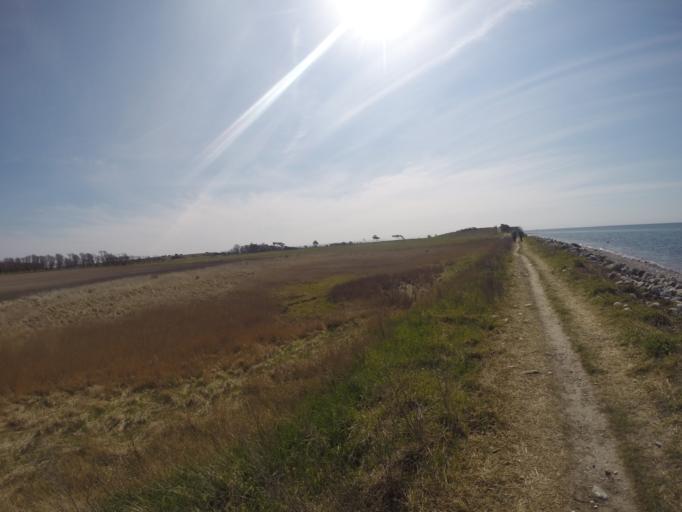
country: DK
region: Zealand
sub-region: Kalundborg Kommune
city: Gorlev
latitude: 55.5181
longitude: 11.0825
